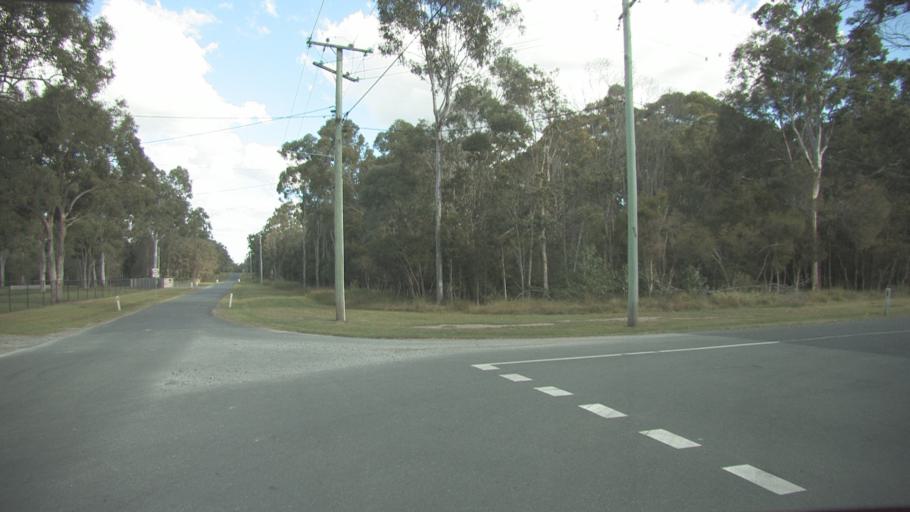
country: AU
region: Queensland
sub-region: Gold Coast
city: Yatala
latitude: -27.6613
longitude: 153.2413
